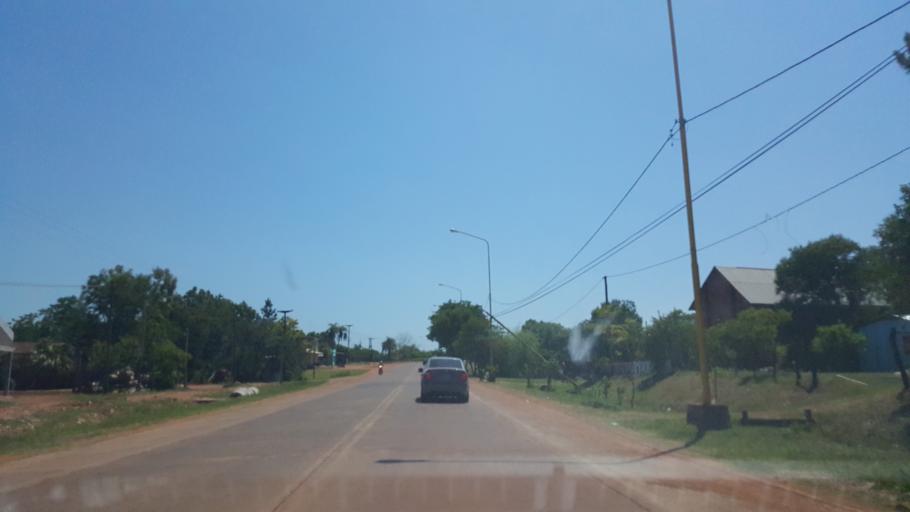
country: AR
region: Corrientes
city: Santo Tome
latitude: -28.5483
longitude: -56.0636
